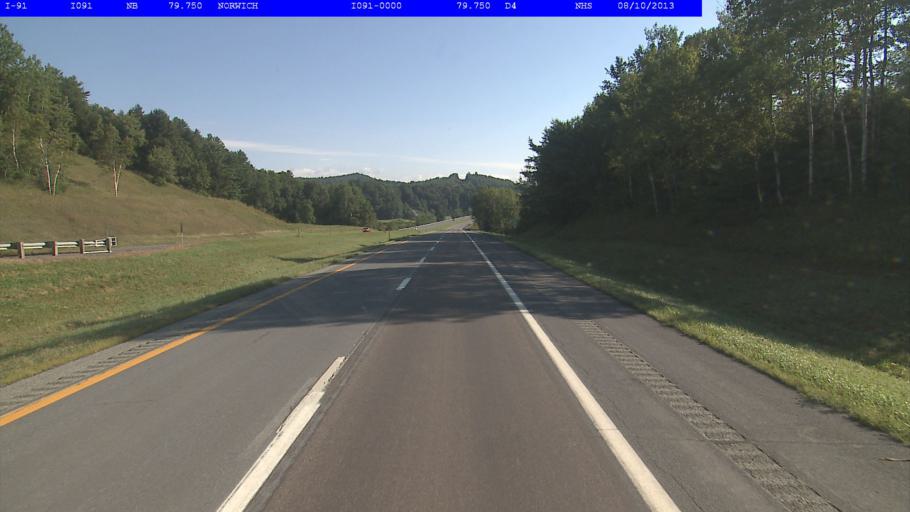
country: US
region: New Hampshire
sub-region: Grafton County
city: Hanover
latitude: 43.7545
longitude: -72.2380
